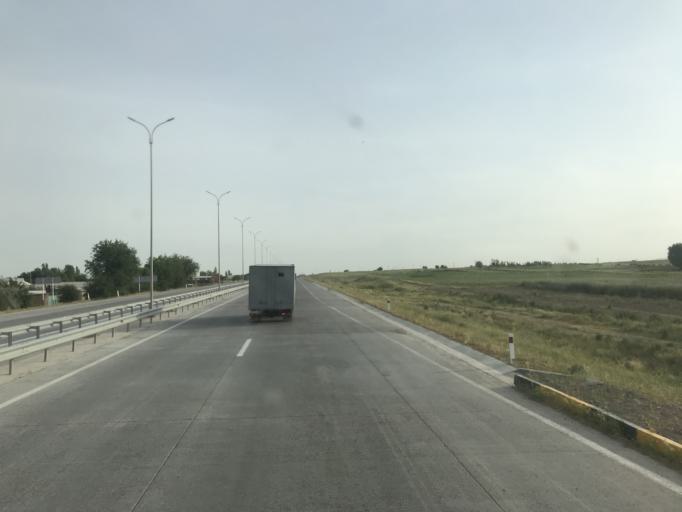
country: UZ
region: Toshkent
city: Qibray
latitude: 41.5564
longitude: 69.4079
